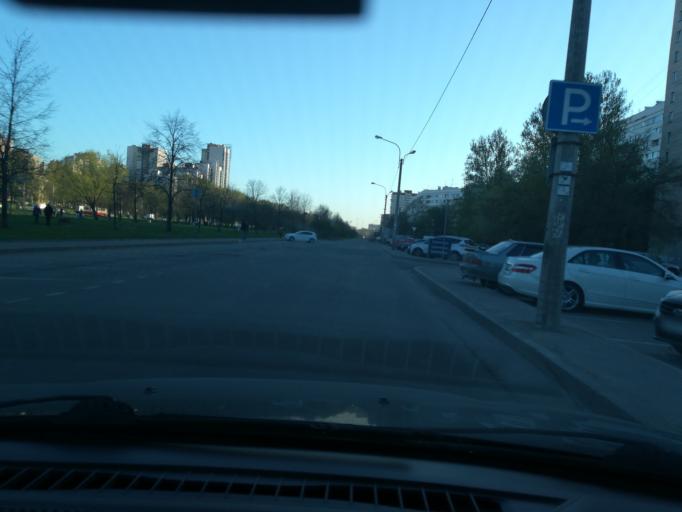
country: RU
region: St.-Petersburg
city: Dachnoye
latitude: 59.8579
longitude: 30.2478
